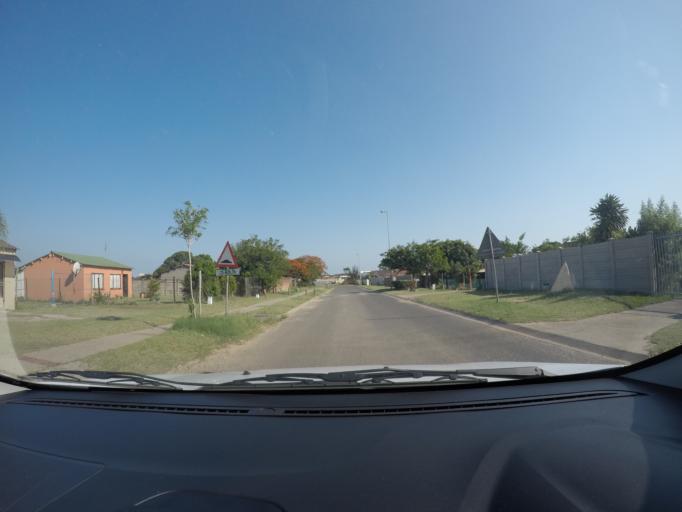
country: ZA
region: KwaZulu-Natal
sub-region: uThungulu District Municipality
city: Richards Bay
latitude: -28.7145
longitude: 32.0336
